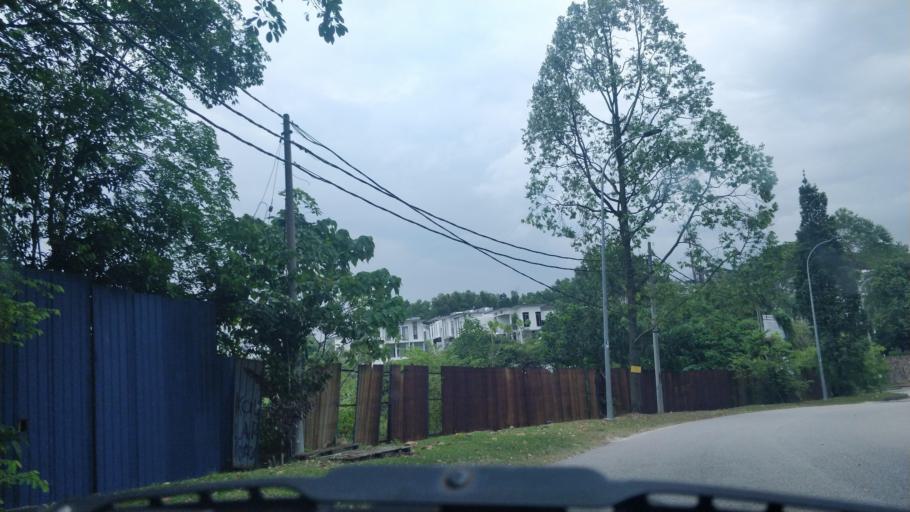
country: MY
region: Selangor
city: Kuang
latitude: 3.2067
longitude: 101.5850
